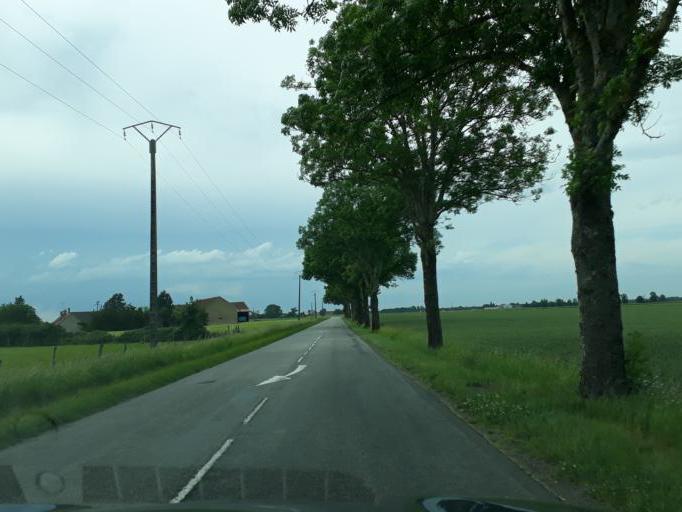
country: FR
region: Centre
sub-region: Departement du Loiret
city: Vienne-en-Val
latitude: 47.8182
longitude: 2.1663
